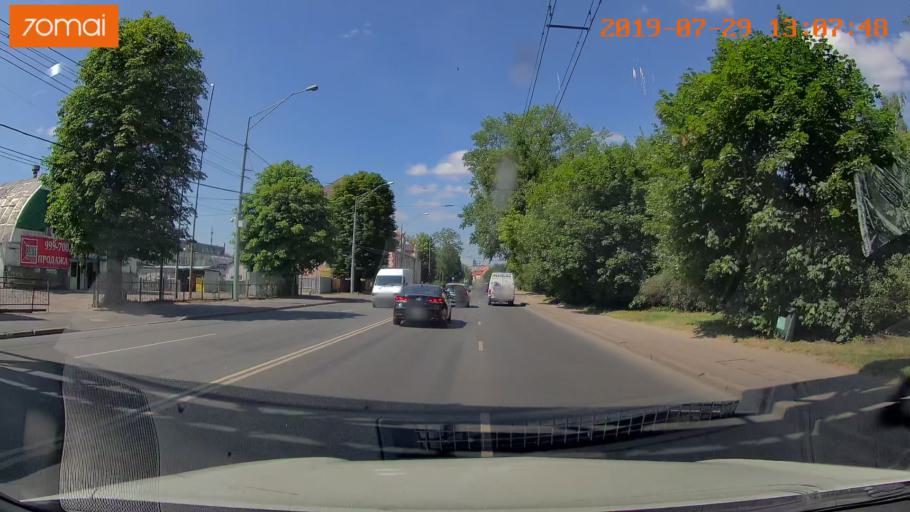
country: RU
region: Kaliningrad
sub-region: Gorod Kaliningrad
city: Kaliningrad
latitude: 54.7110
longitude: 20.4399
